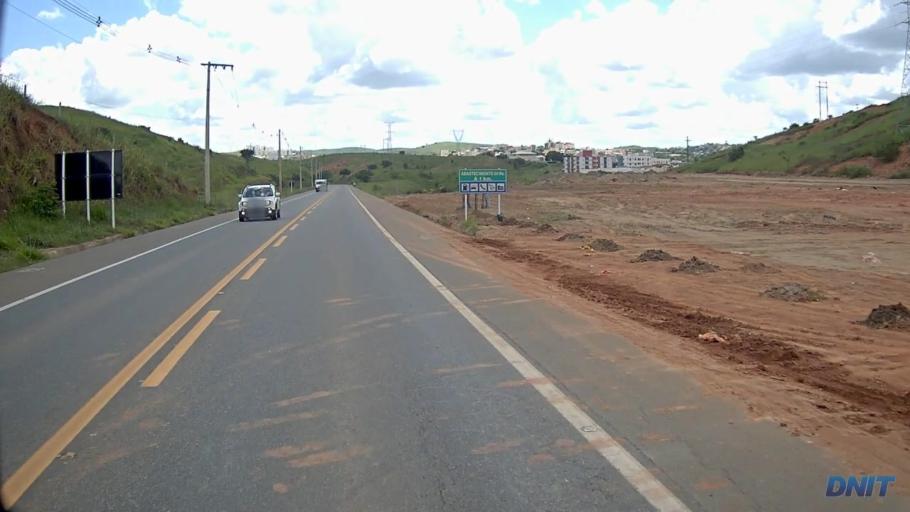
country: BR
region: Minas Gerais
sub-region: Governador Valadares
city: Governador Valadares
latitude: -18.8481
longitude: -41.9830
